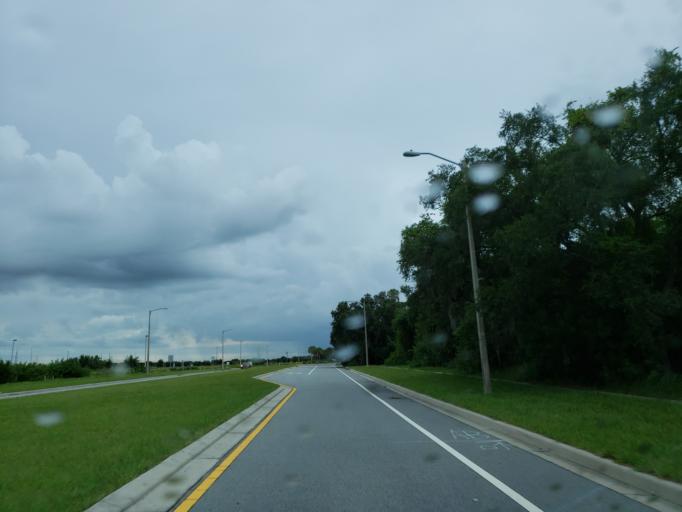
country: US
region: Florida
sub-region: Hillsborough County
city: Sun City Center
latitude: 27.7290
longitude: -82.3917
